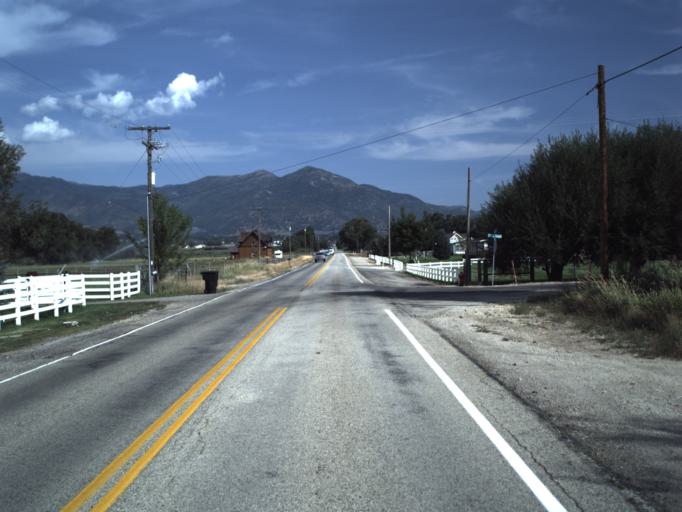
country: US
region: Utah
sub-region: Wasatch County
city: Midway
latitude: 40.4704
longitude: -111.4718
